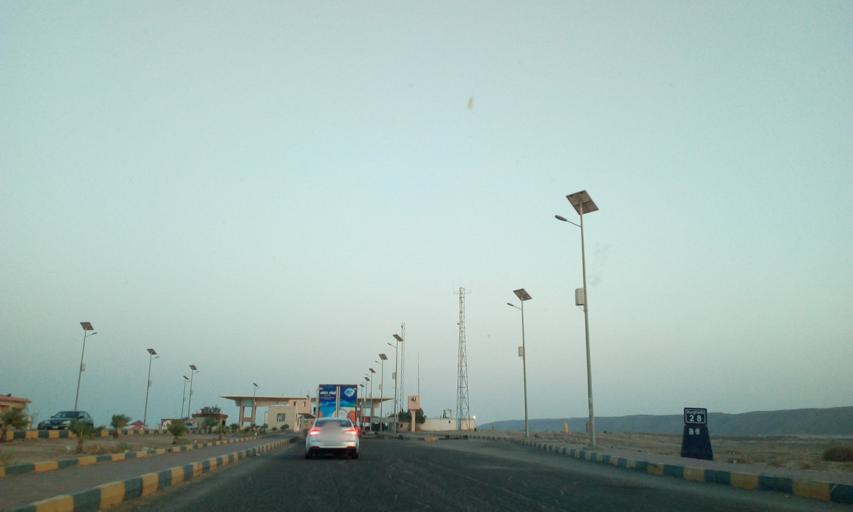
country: EG
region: Red Sea
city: El Gouna
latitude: 27.4214
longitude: 33.6143
